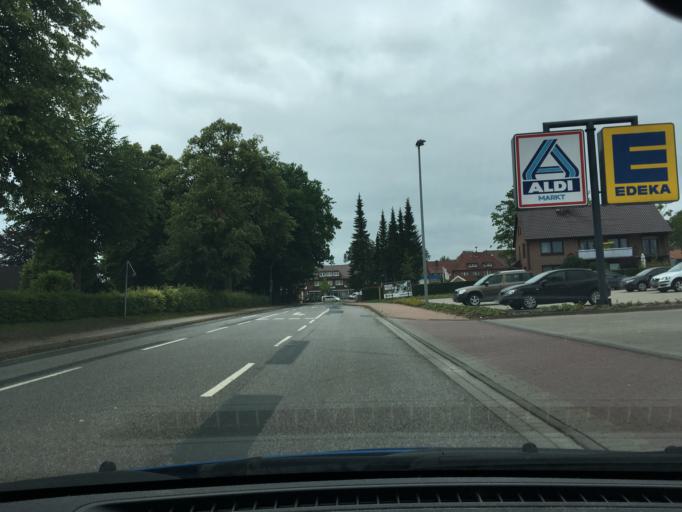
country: DE
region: Lower Saxony
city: Buchholz in der Nordheide
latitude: 53.3782
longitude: 9.8972
